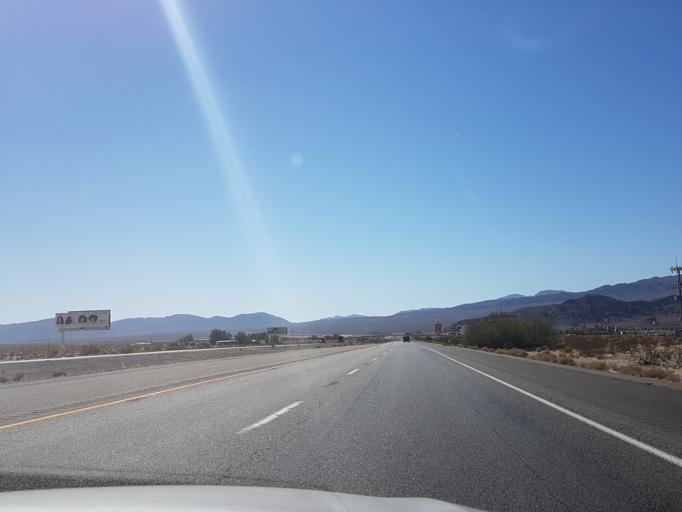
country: US
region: California
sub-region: San Bernardino County
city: Fort Irwin
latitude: 35.2727
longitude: -116.0589
